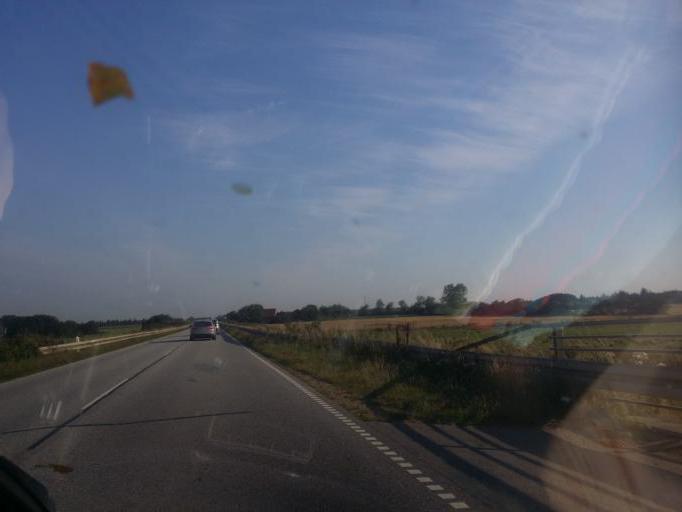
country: DK
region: South Denmark
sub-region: Tonder Kommune
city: Sherrebek
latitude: 55.2387
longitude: 8.7239
